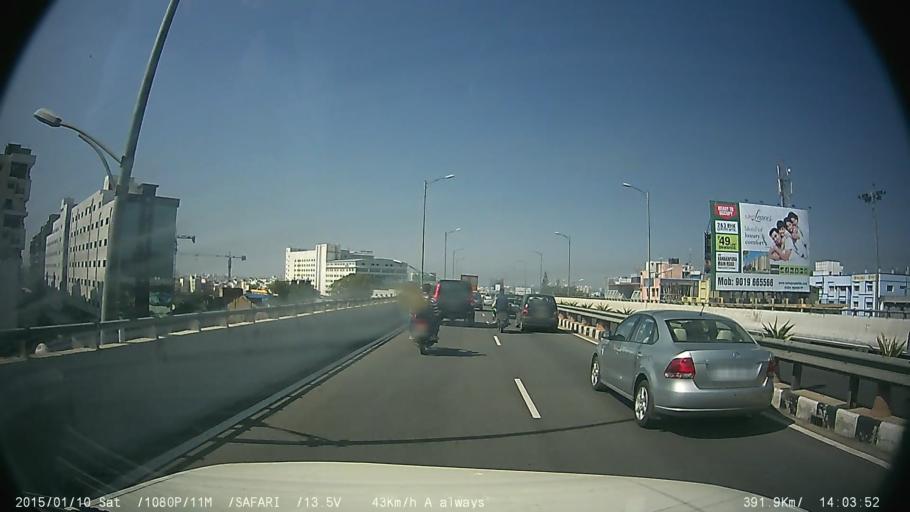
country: IN
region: Karnataka
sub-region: Bangalore Urban
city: Bangalore
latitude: 12.8888
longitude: 77.6399
